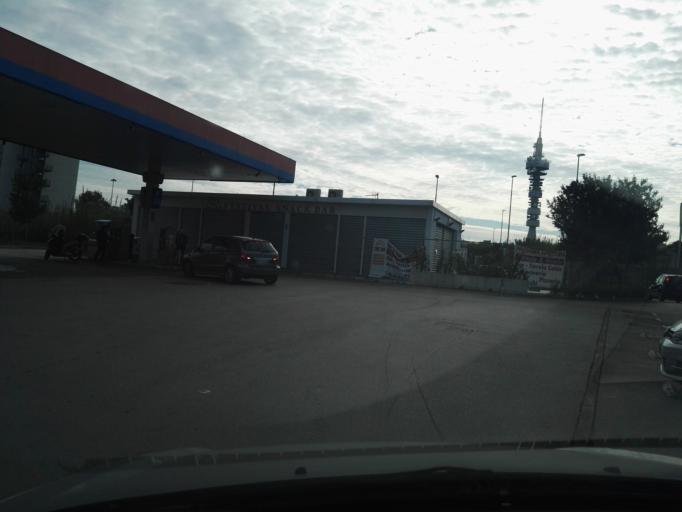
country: IT
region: Latium
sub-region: Citta metropolitana di Roma Capitale
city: Selcetta
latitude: 41.8003
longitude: 12.4812
